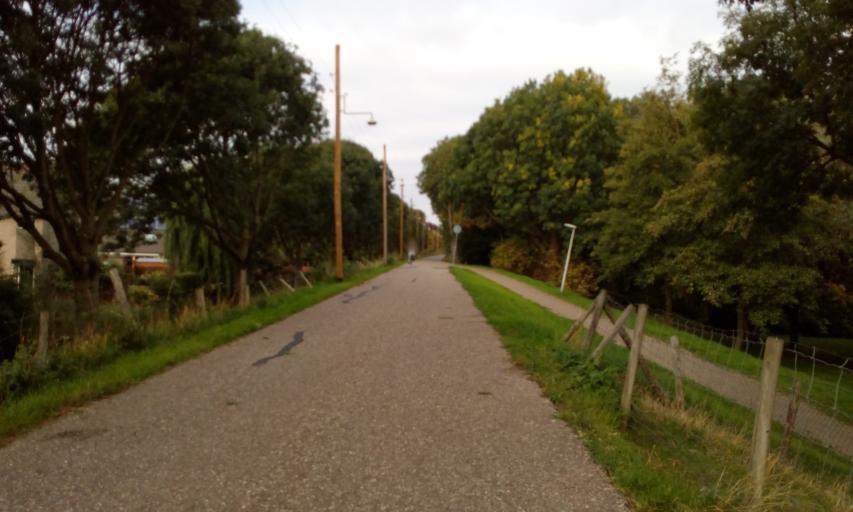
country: NL
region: South Holland
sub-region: Gemeente Spijkenisse
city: Spijkenisse
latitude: 51.8572
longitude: 4.3701
